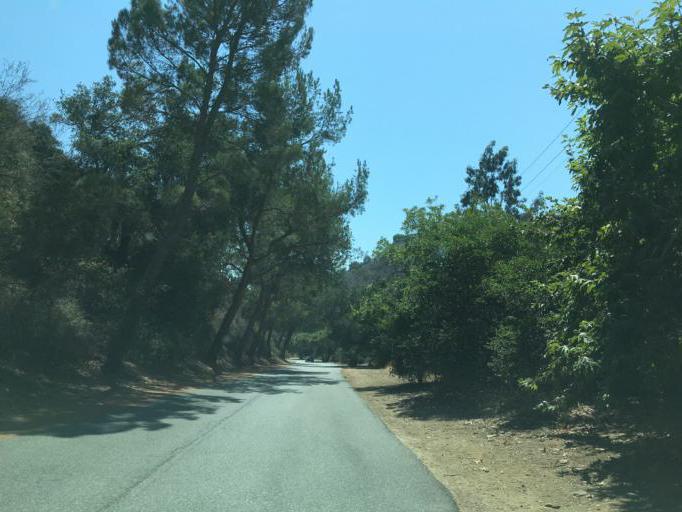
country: US
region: California
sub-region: Los Angeles County
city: Beverly Hills
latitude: 34.1090
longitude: -118.4155
